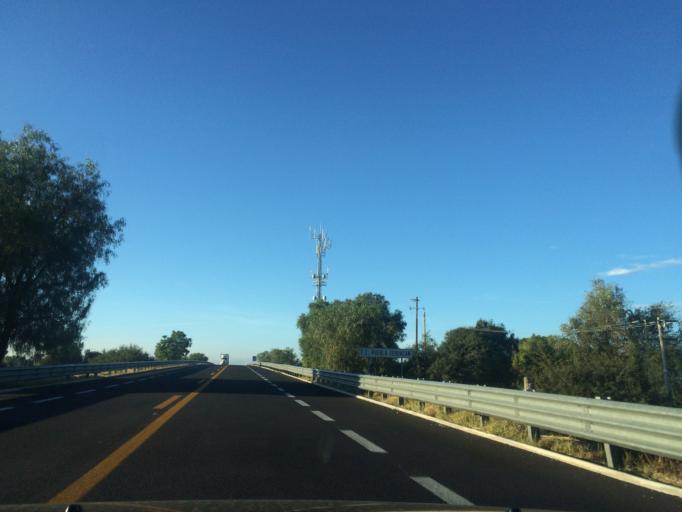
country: MX
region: Puebla
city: Santiago Miahuatlan
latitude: 18.5356
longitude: -97.4586
